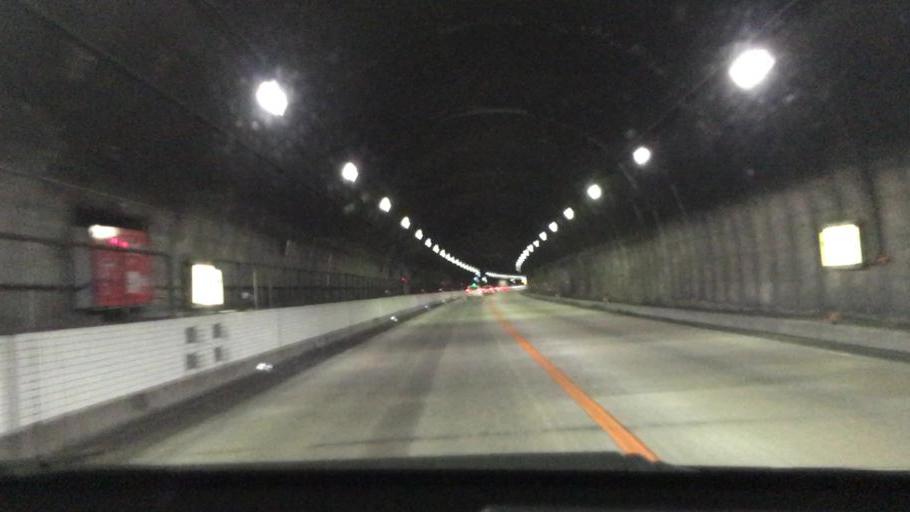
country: JP
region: Yamaguchi
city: Tokuyama
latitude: 34.0861
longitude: 131.7463
